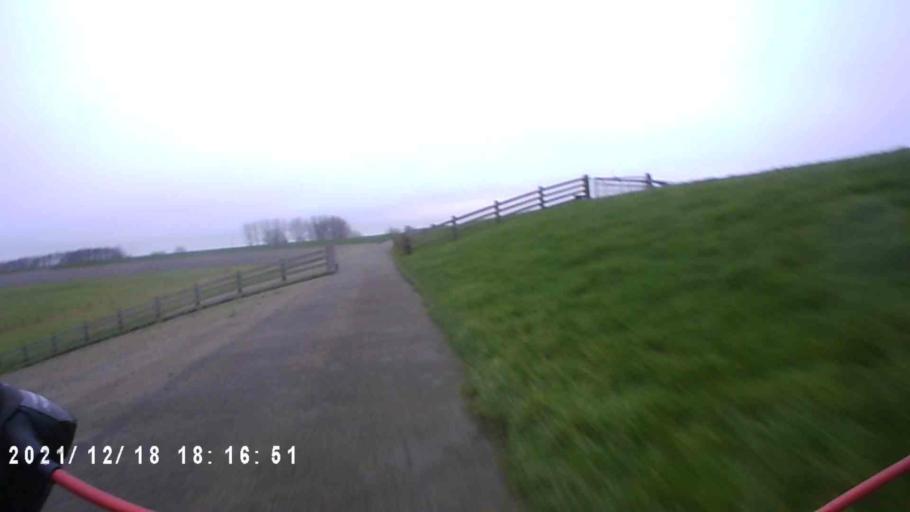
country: NL
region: Friesland
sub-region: Gemeente Dongeradeel
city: Ternaard
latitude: 53.3937
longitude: 5.9700
